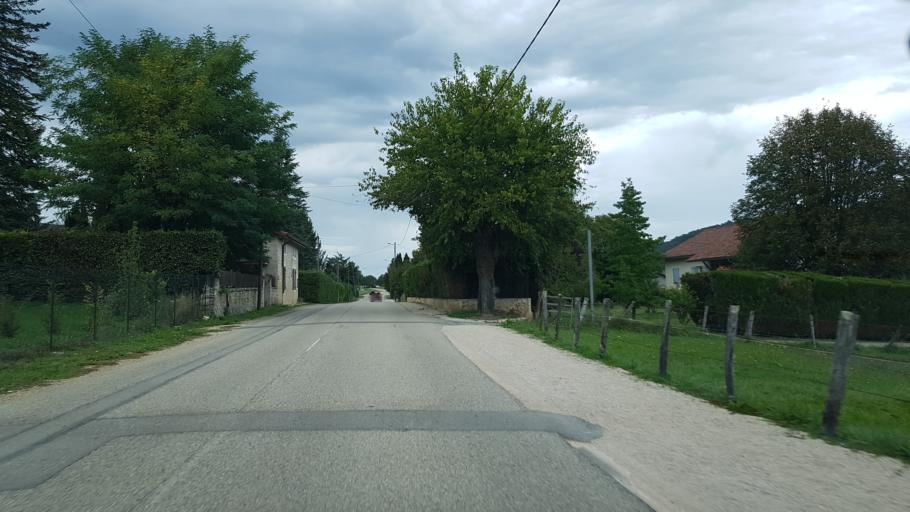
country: FR
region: Rhone-Alpes
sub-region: Departement de l'Ain
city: Cuisiat
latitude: 46.2665
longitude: 5.4263
